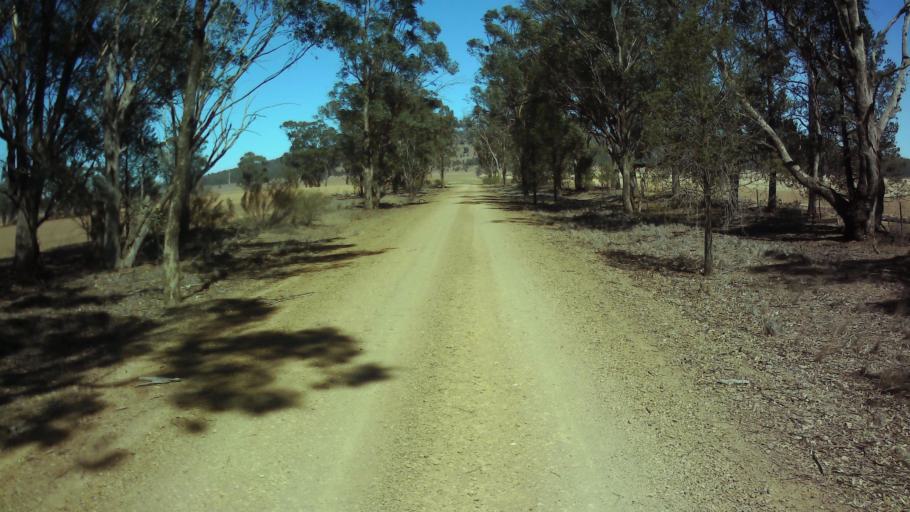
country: AU
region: New South Wales
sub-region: Weddin
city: Grenfell
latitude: -33.7044
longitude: 147.9736
